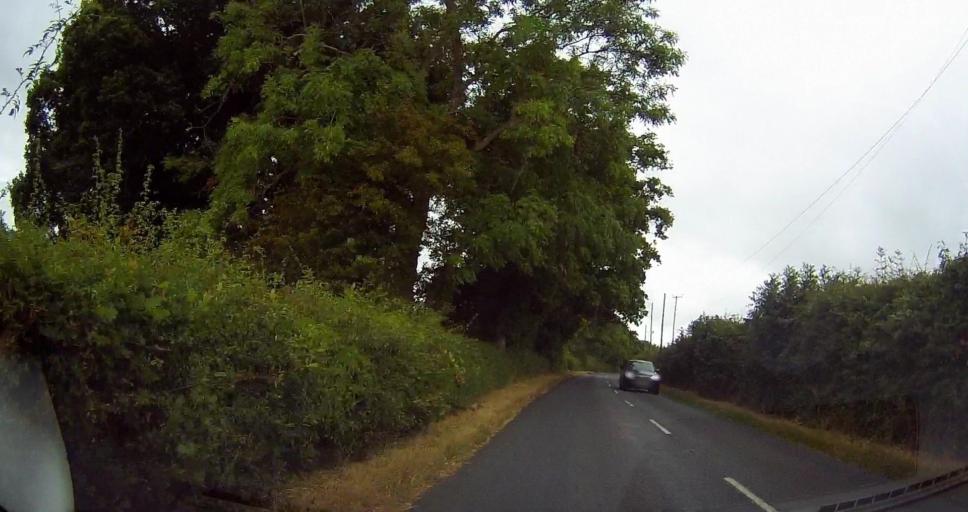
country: GB
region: England
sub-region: East Sussex
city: Wadhurst
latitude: 51.0846
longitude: 0.3811
